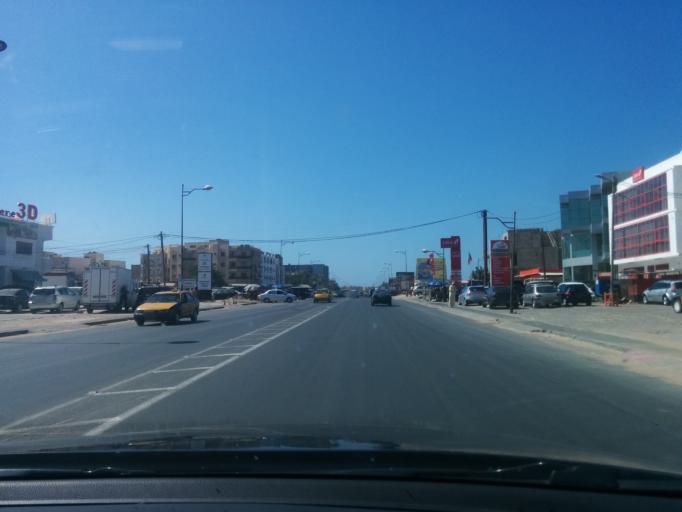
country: SN
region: Dakar
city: Mermoz Boabab
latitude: 14.7133
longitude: -17.4754
